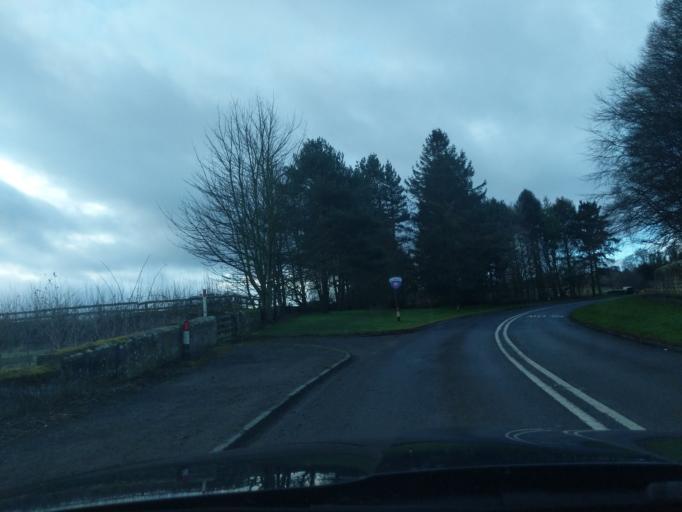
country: GB
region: England
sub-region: Northumberland
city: Alnwick
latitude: 55.4175
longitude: -1.6897
